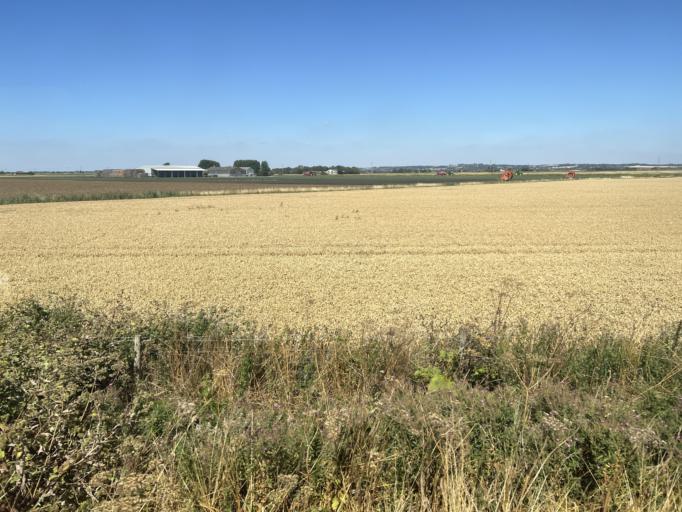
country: GB
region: England
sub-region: Lincolnshire
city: Spilsby
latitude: 53.1062
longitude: 0.1182
